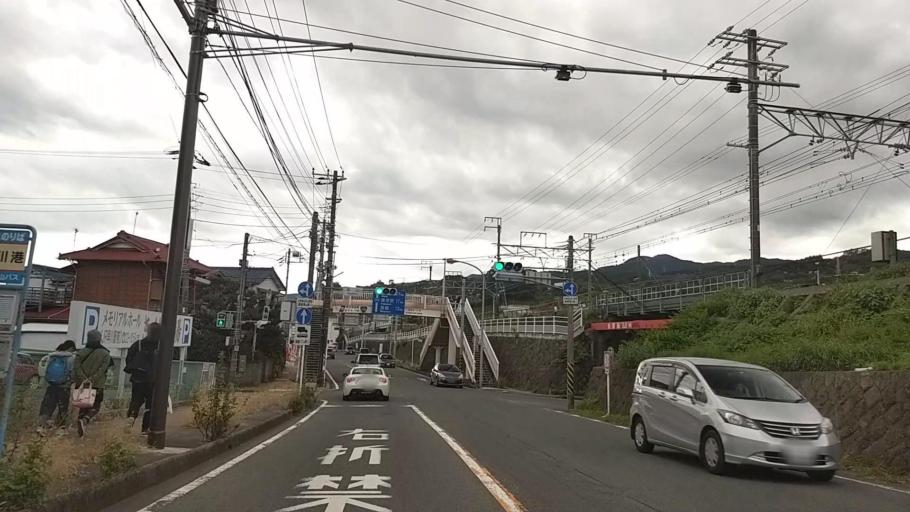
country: JP
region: Kanagawa
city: Odawara
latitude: 35.2415
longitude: 139.1465
